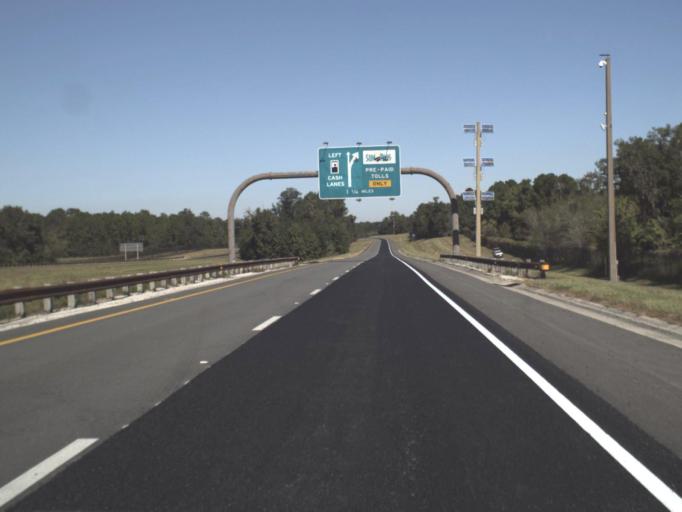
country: US
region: Florida
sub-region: Hernando County
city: Brookridge
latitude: 28.6358
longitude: -82.4890
